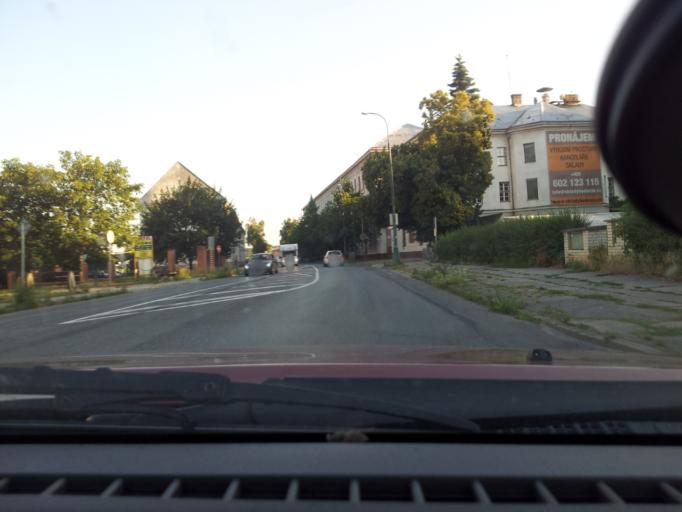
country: CZ
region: South Moravian
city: Hodonin
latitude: 48.8453
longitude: 17.1262
